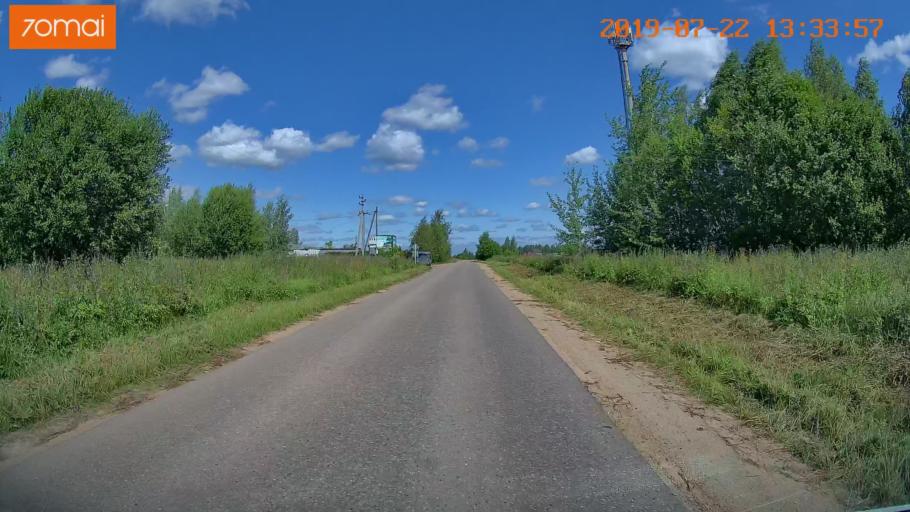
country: RU
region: Ivanovo
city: Novo-Talitsy
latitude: 57.0601
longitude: 40.8793
